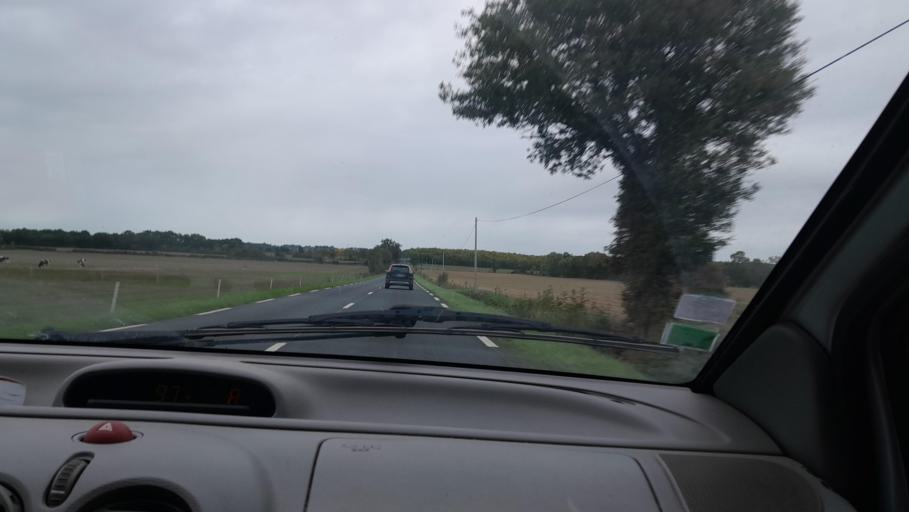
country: FR
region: Pays de la Loire
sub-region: Departement de la Loire-Atlantique
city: Saint-Mars-la-Jaille
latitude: 47.4752
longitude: -1.1745
